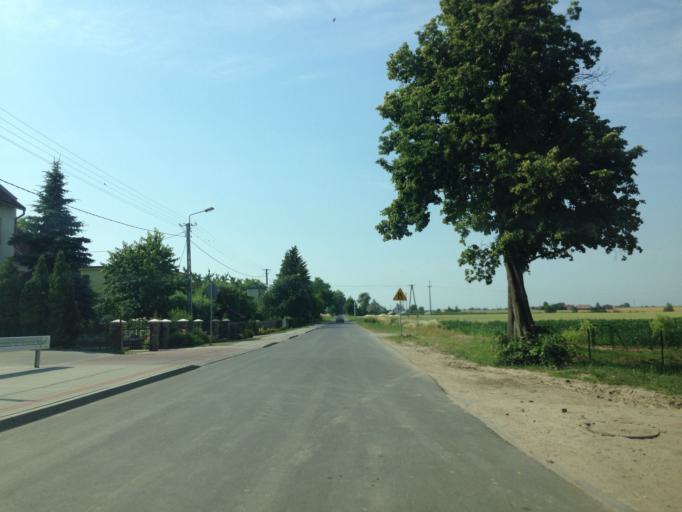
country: PL
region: Kujawsko-Pomorskie
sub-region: Powiat brodnicki
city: Bobrowo
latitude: 53.2324
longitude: 19.2558
